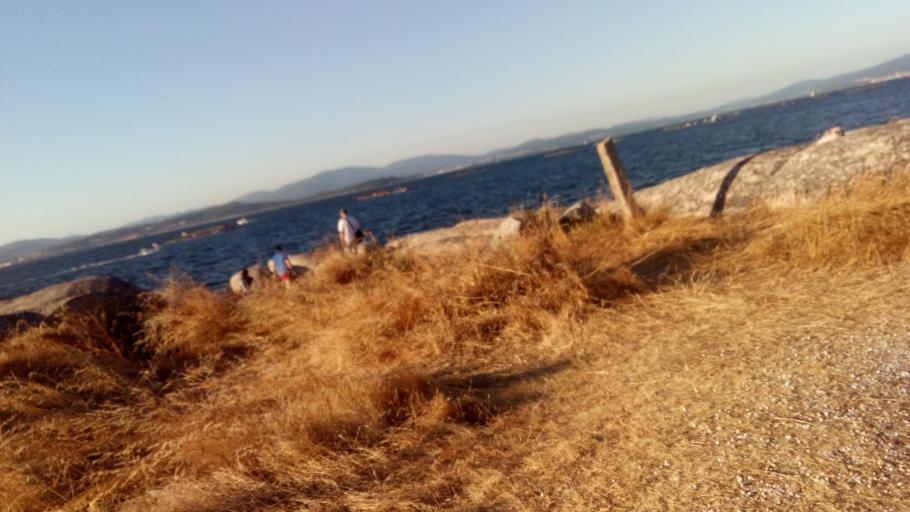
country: ES
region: Galicia
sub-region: Provincia de Pontevedra
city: Vilanova de Arousa
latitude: 42.5725
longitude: -8.8841
